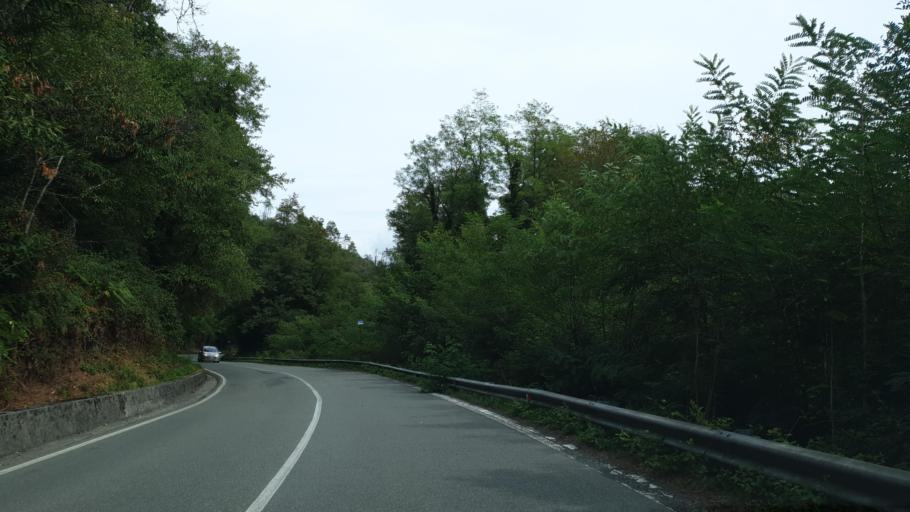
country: IT
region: Liguria
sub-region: Provincia di La Spezia
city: Carrodano
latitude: 44.2251
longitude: 9.6303
